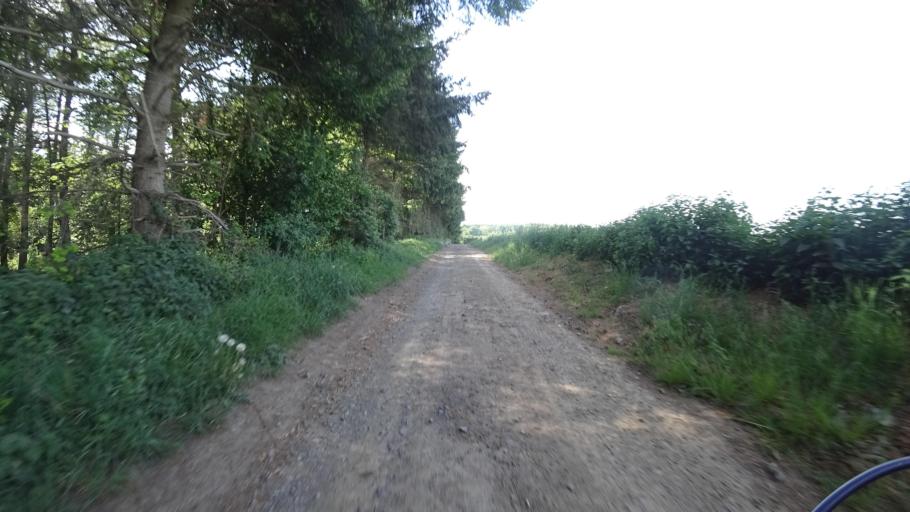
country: BE
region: Wallonia
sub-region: Province de Namur
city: Namur
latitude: 50.4997
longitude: 4.8196
